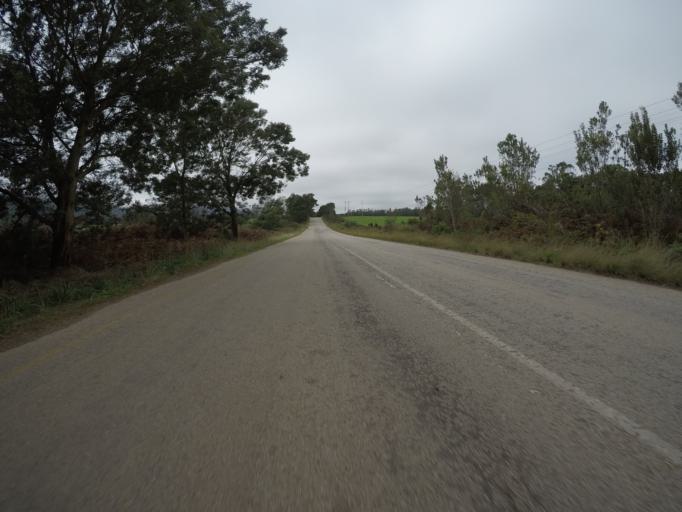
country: ZA
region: Eastern Cape
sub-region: Cacadu District Municipality
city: Kareedouw
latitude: -33.9967
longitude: 24.1485
